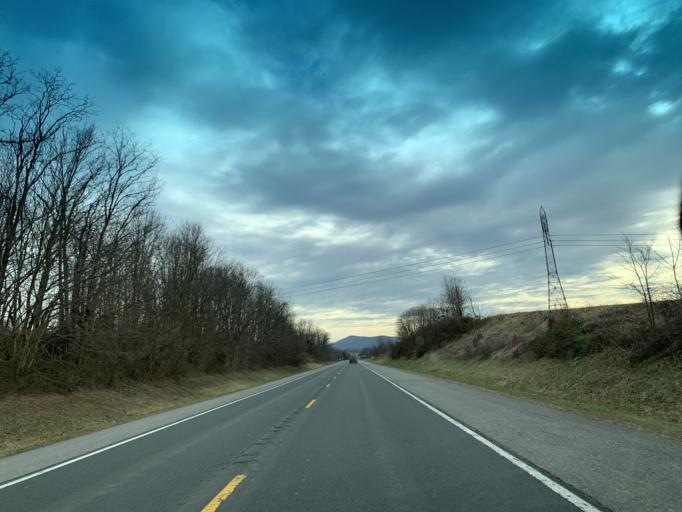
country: US
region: Maryland
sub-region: Washington County
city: Boonsboro
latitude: 39.4772
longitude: -77.6538
